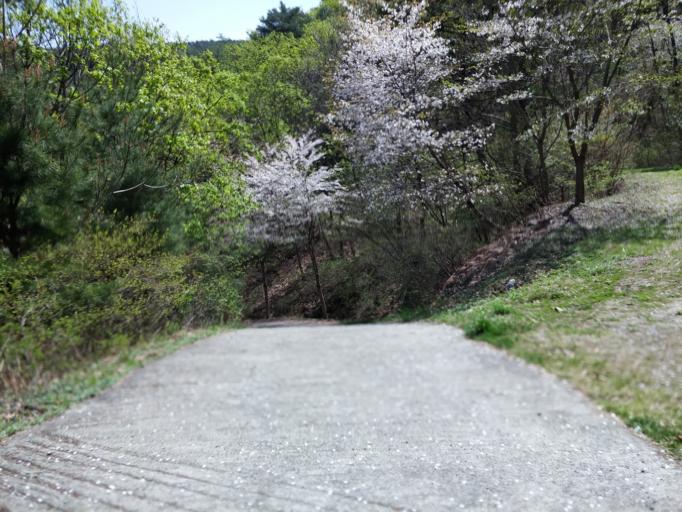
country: KR
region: Daejeon
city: Daejeon
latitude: 36.2753
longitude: 127.4837
